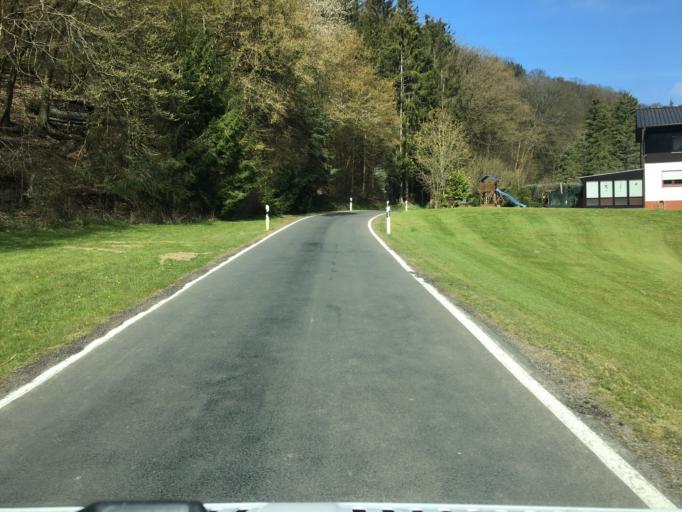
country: DE
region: Rheinland-Pfalz
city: Kirchsahr
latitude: 50.5141
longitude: 6.9036
